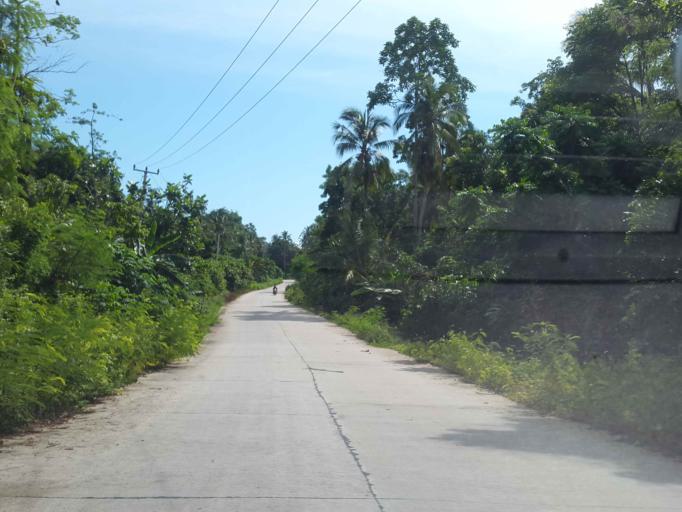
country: ID
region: Banten
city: Babakanbungur
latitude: -6.5292
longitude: 105.6265
